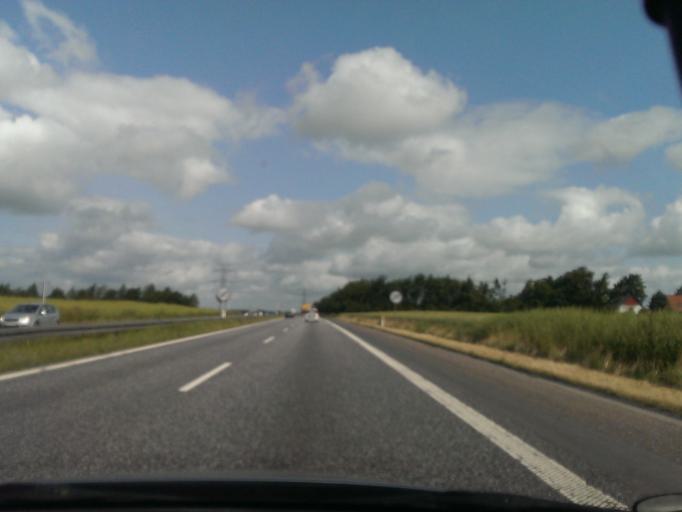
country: DK
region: Central Jutland
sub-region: Randers Kommune
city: Randers
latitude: 56.4971
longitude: 9.9790
